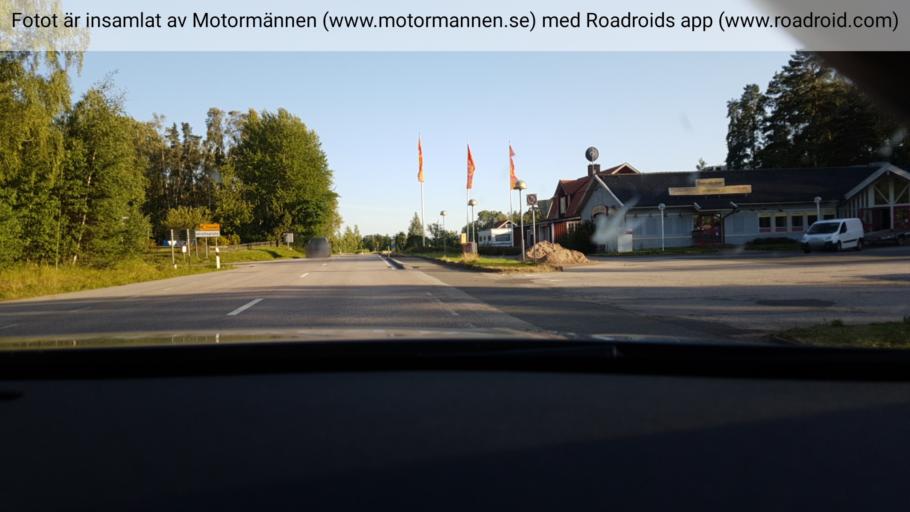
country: SE
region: Vaestra Goetaland
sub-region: Skovde Kommun
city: Stopen
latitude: 58.5026
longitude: 13.9705
